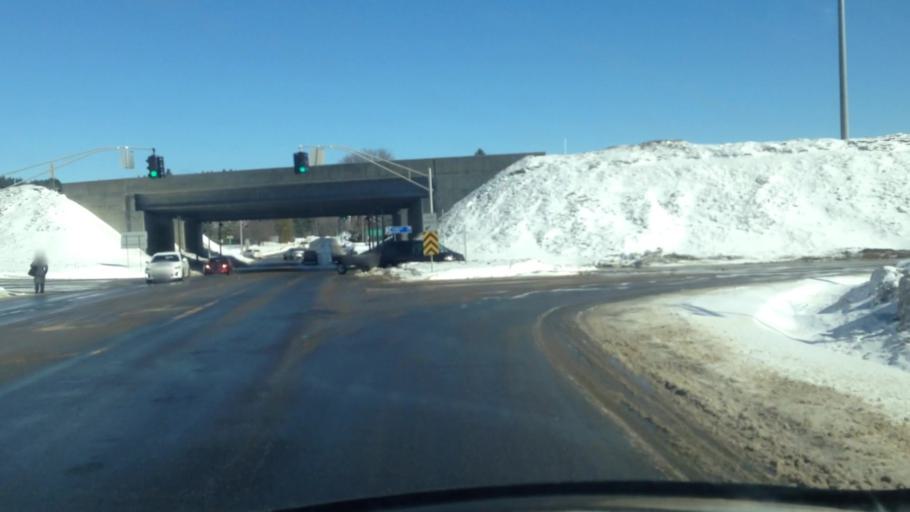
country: CA
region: Quebec
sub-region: Laurentides
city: Mont-Tremblant
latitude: 46.1141
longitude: -74.6060
